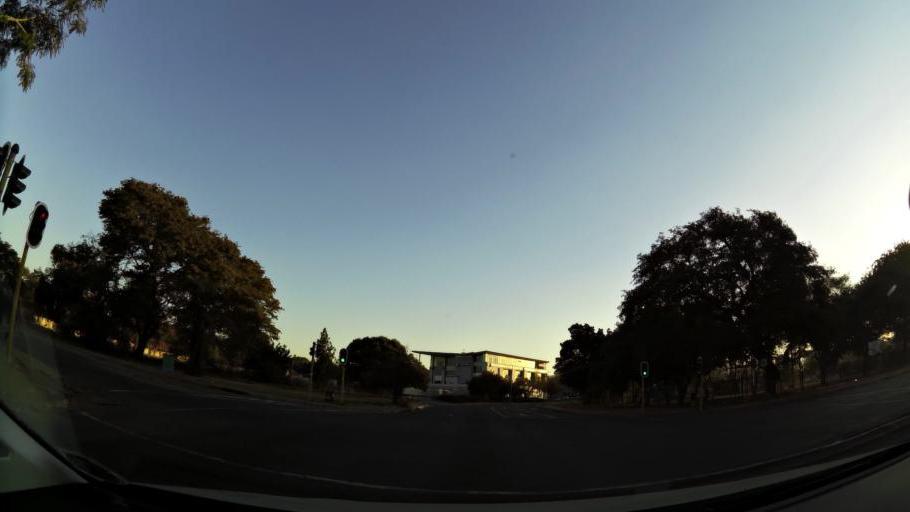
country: ZA
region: North-West
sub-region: Bojanala Platinum District Municipality
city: Rustenburg
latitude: -25.6753
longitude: 27.2482
